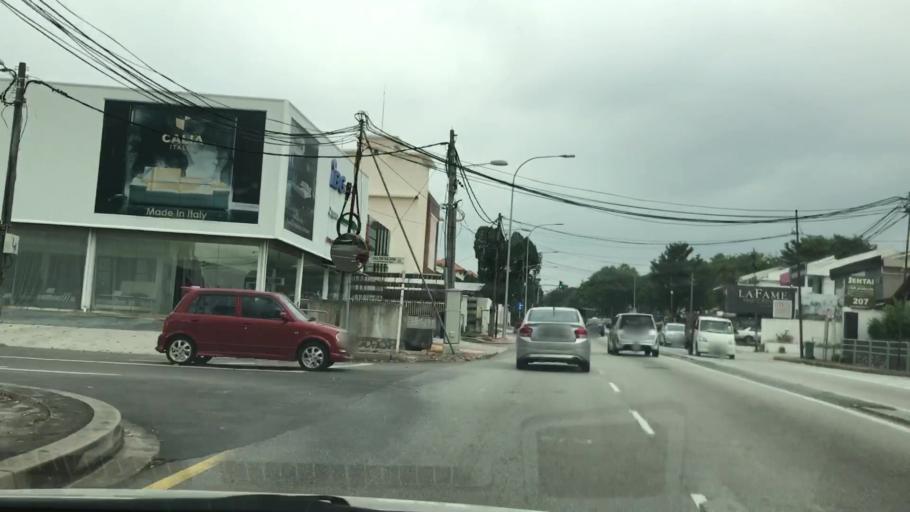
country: MY
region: Selangor
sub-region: Petaling
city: Petaling Jaya
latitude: 3.1181
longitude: 101.6257
